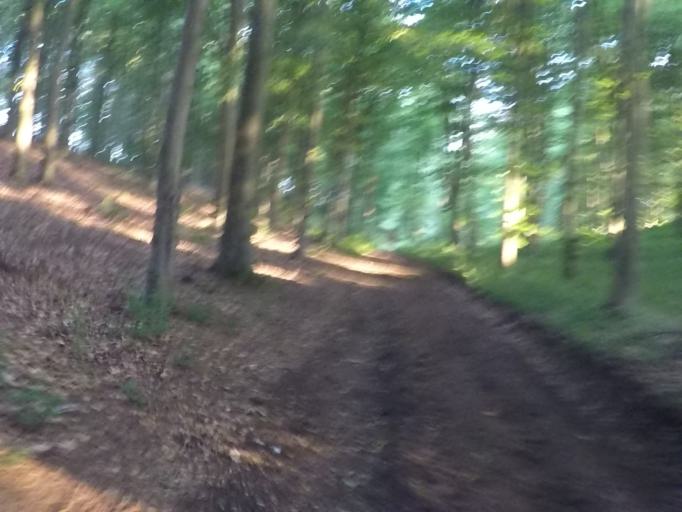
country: GB
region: England
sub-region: Oxfordshire
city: Charlbury
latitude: 51.9077
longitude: -1.4958
